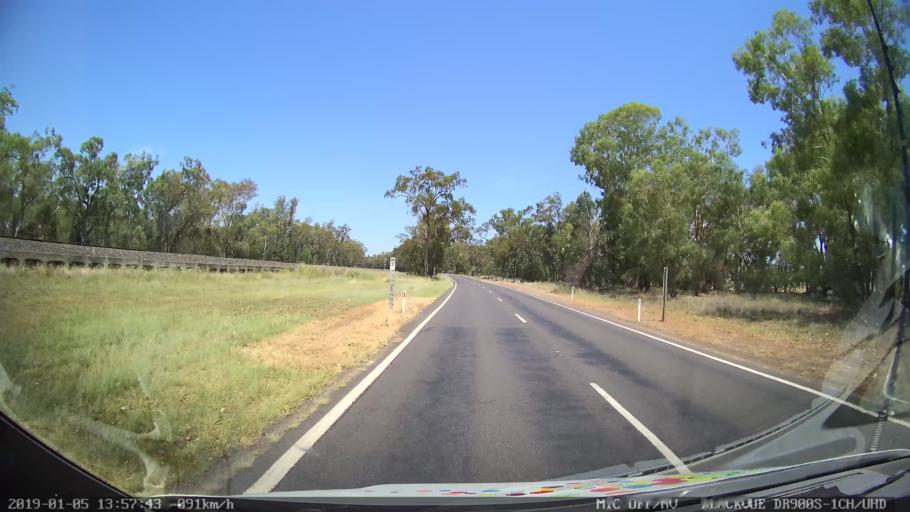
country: AU
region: New South Wales
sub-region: Gunnedah
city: Gunnedah
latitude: -31.1308
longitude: 150.2763
